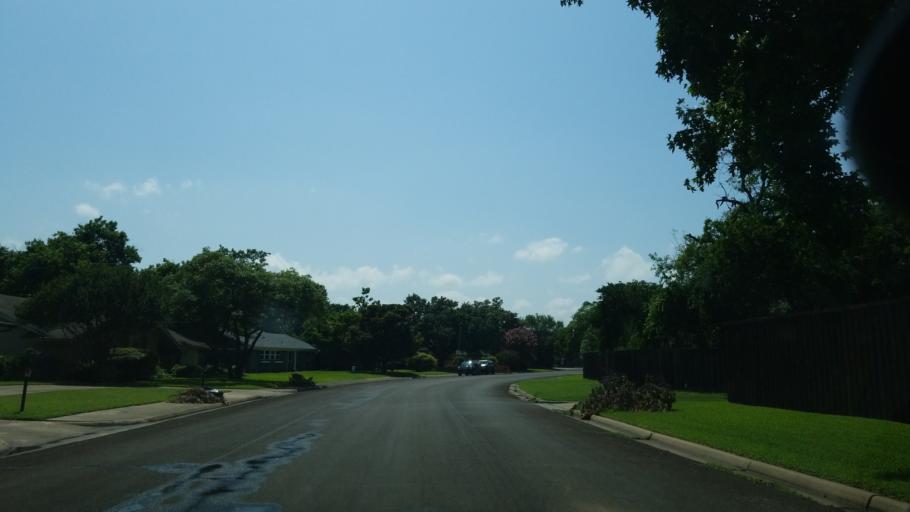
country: US
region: Texas
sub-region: Dallas County
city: Farmers Branch
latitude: 32.8874
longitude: -96.8680
